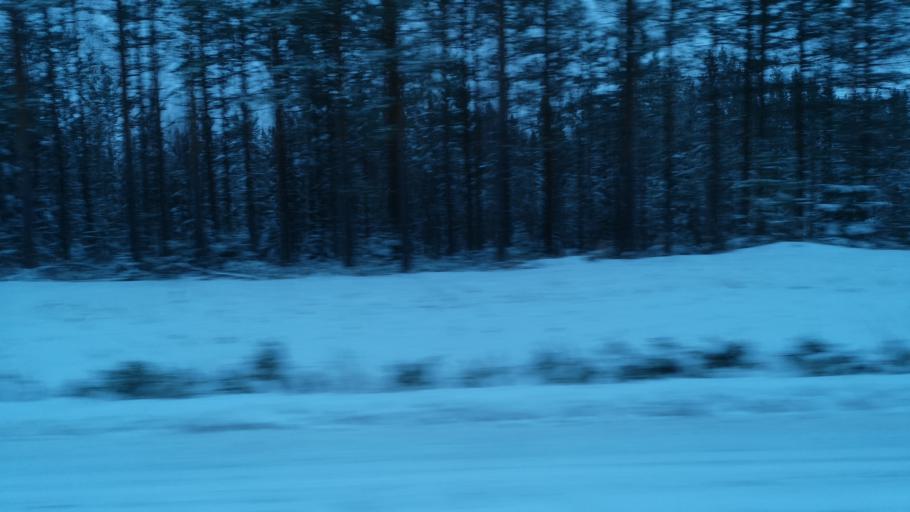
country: FI
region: Southern Savonia
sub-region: Savonlinna
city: Savonlinna
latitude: 61.9704
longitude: 28.8161
